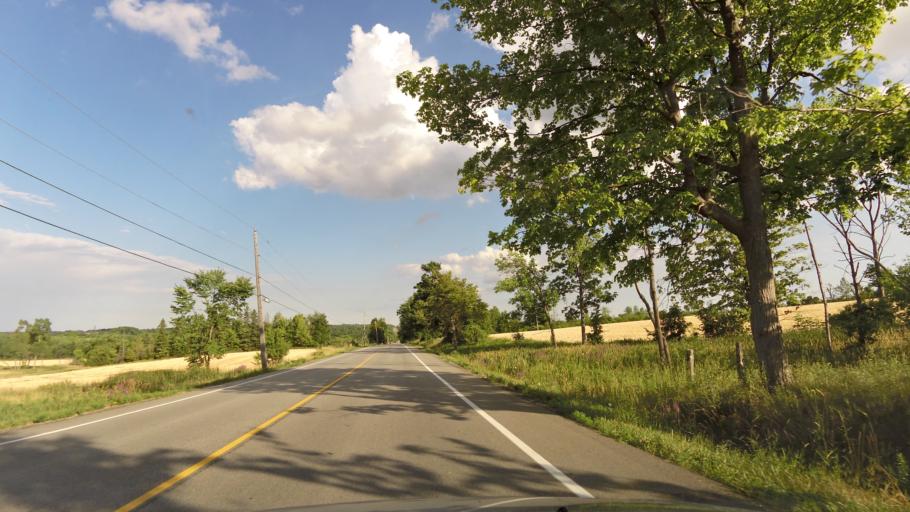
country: CA
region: Ontario
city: Brampton
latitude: 43.7456
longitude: -79.9363
